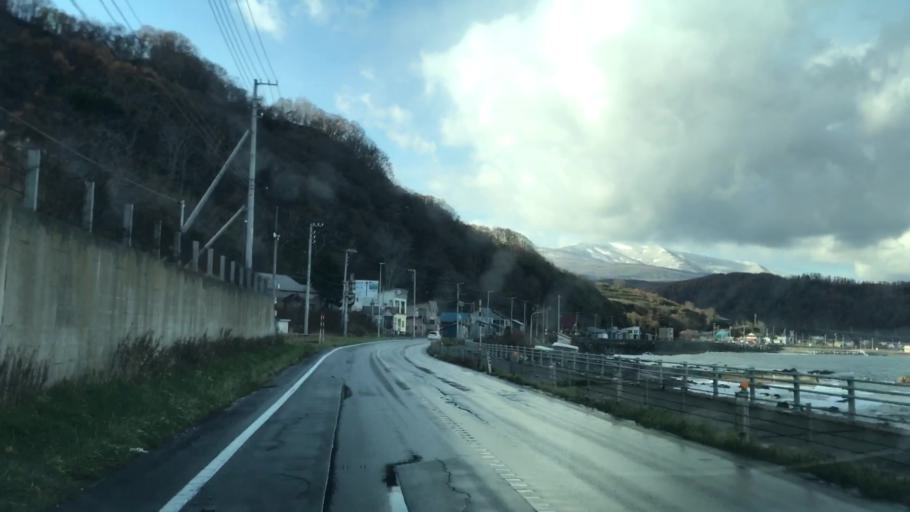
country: JP
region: Hokkaido
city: Yoichi
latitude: 43.2961
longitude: 140.6157
